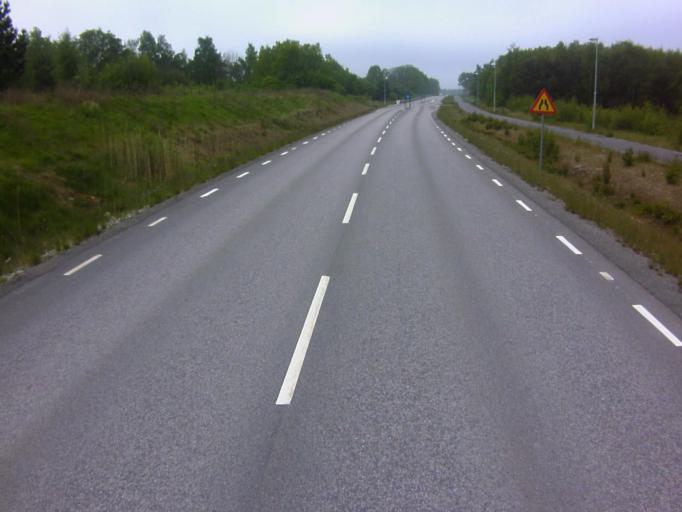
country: SE
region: Blekinge
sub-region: Solvesborgs Kommun
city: Soelvesborg
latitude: 56.0560
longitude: 14.6175
